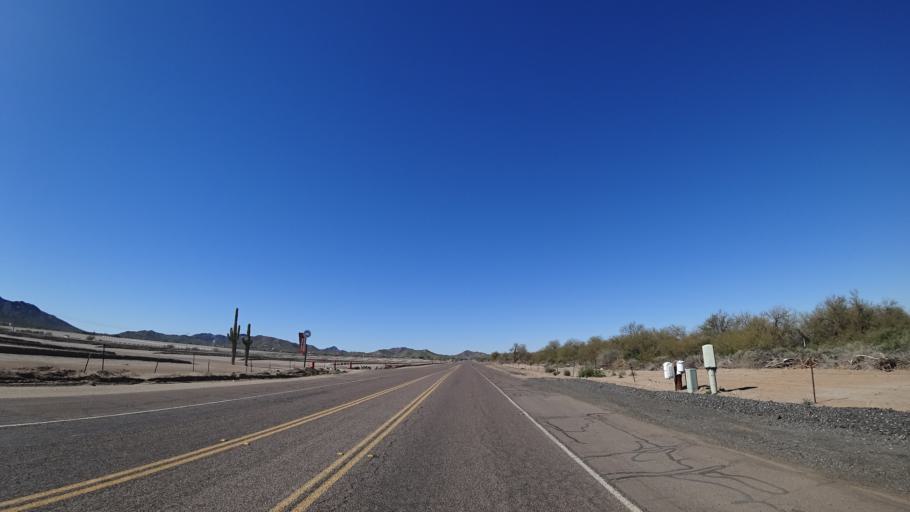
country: US
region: Arizona
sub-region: Maricopa County
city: Avondale
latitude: 33.3756
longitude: -112.3245
